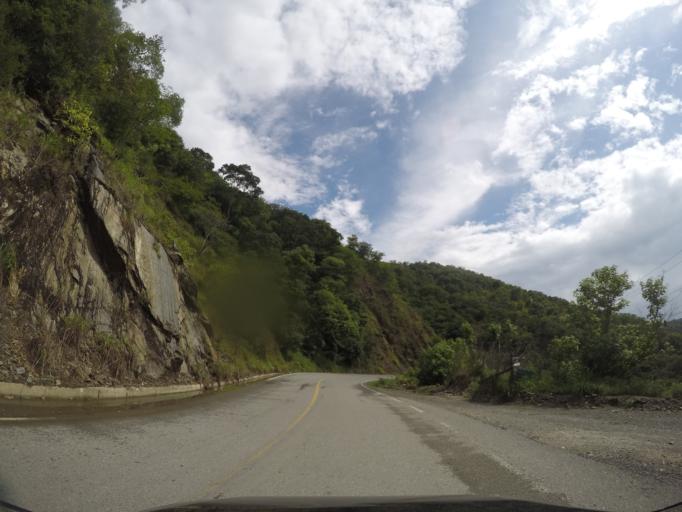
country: MX
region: Oaxaca
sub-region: San Jeronimo Coatlan
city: San Cristobal Honduras
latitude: 16.3741
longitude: -97.0791
